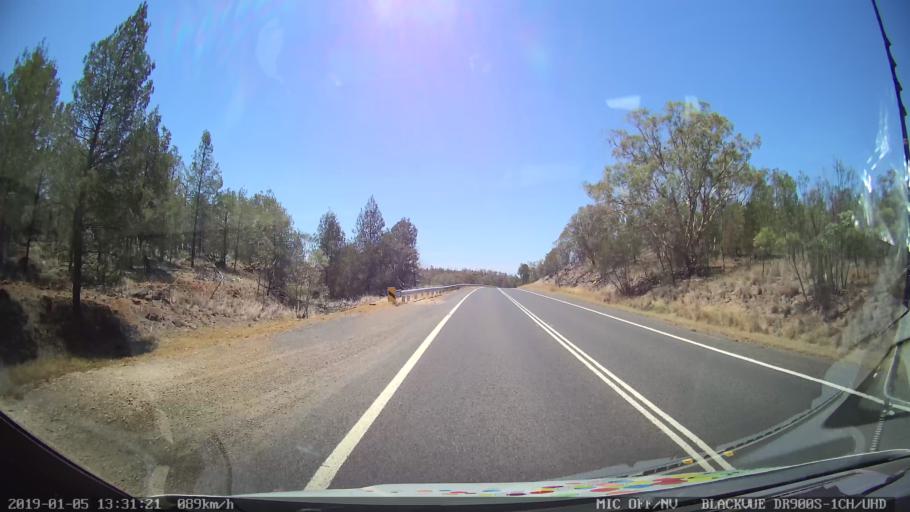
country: AU
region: New South Wales
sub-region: Gunnedah
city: Gunnedah
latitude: -31.0114
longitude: 150.0830
